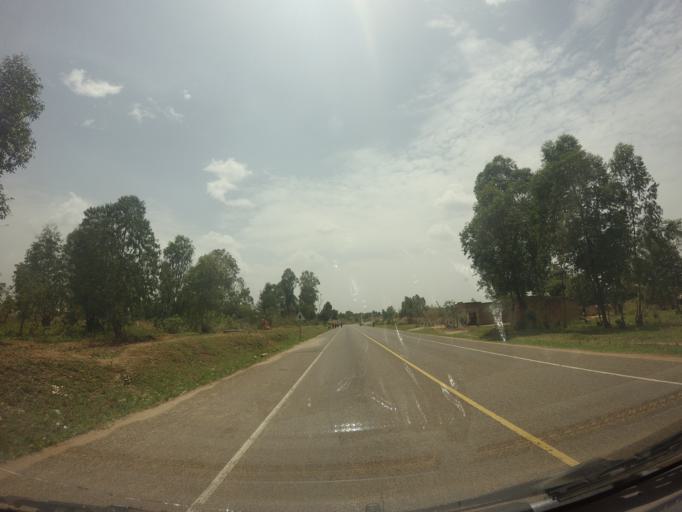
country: UG
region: Northern Region
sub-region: Arua District
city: Arua
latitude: 2.9547
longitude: 30.9151
